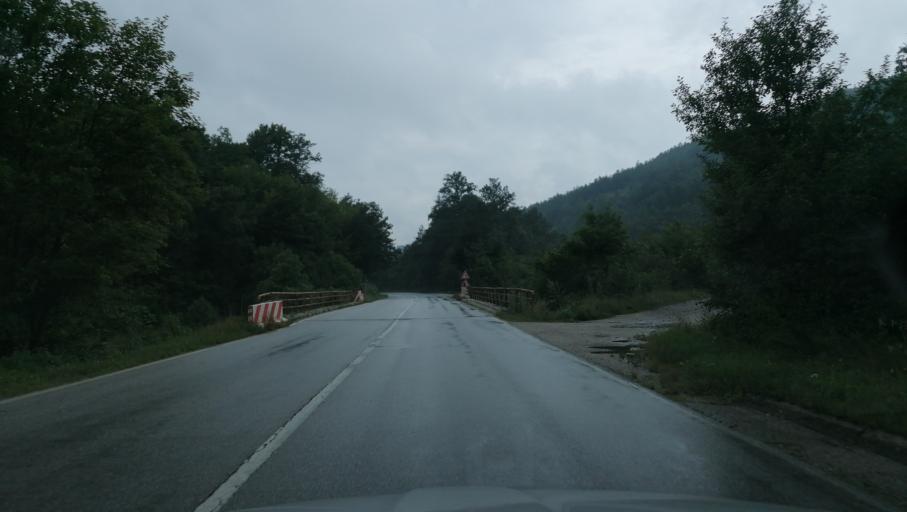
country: RS
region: Central Serbia
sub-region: Zlatiborski Okrug
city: Cajetina
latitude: 43.7898
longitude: 19.7123
